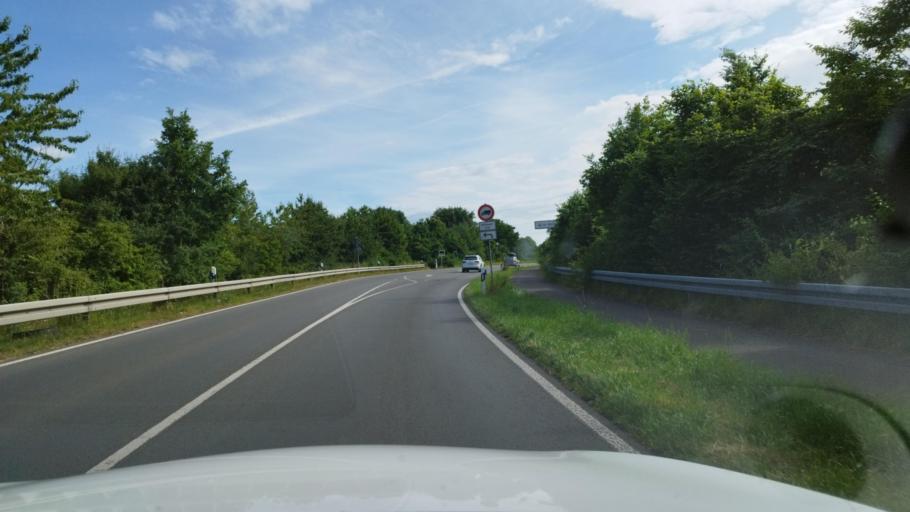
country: DE
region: North Rhine-Westphalia
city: Waltrop
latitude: 51.6306
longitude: 7.4259
